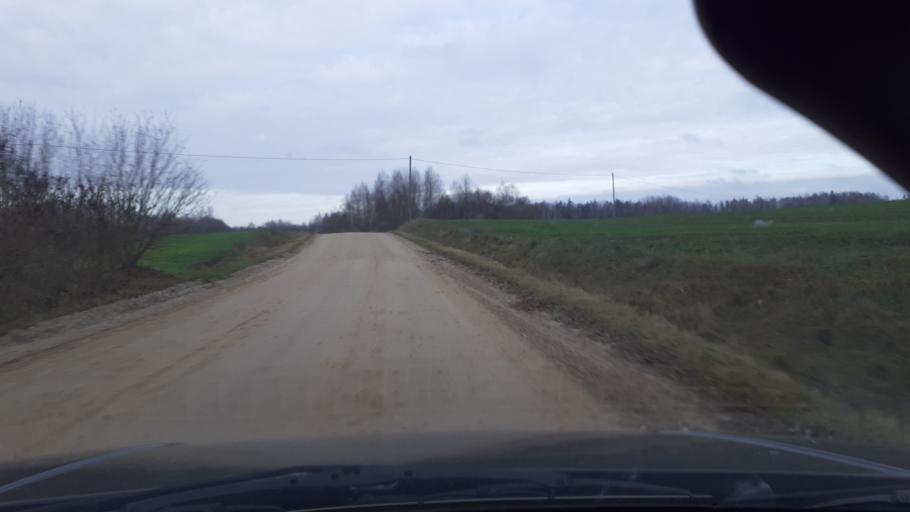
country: LV
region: Alsunga
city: Alsunga
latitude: 56.9530
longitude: 21.6484
